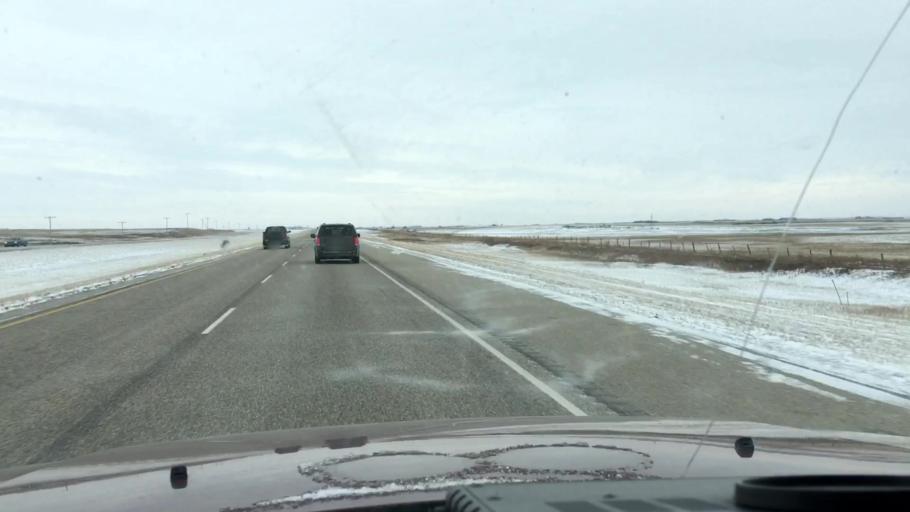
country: CA
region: Saskatchewan
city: Saskatoon
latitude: 51.5959
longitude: -106.3905
